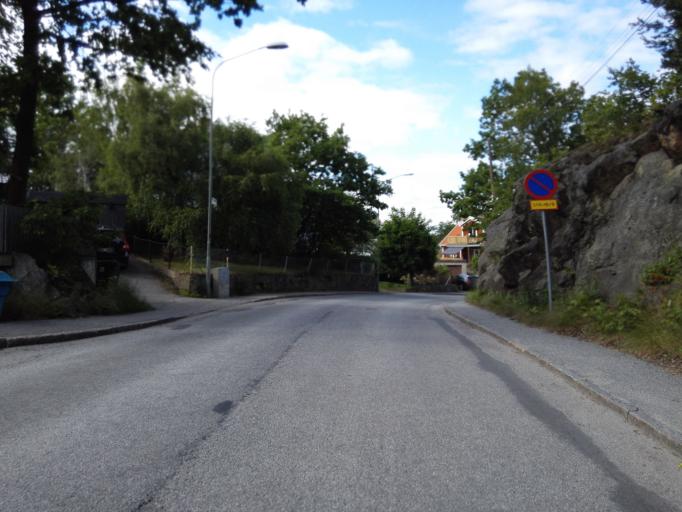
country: SE
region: Stockholm
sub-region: Huddinge Kommun
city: Huddinge
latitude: 59.2668
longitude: 17.9848
